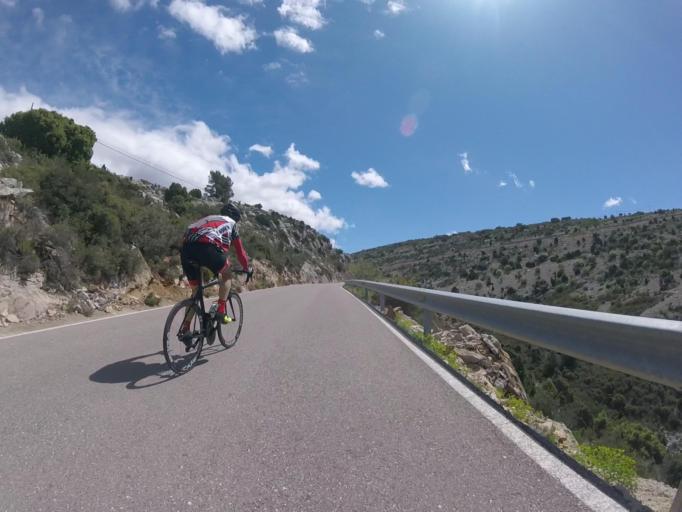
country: ES
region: Valencia
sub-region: Provincia de Castello
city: Sierra-Engarceran
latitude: 40.2789
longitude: -0.0326
